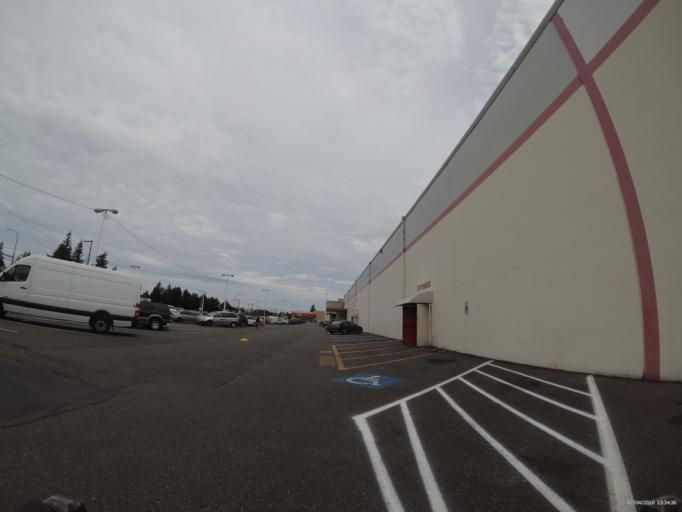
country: US
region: Washington
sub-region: Pierce County
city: McChord Air Force Base
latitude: 47.1570
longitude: -122.4900
